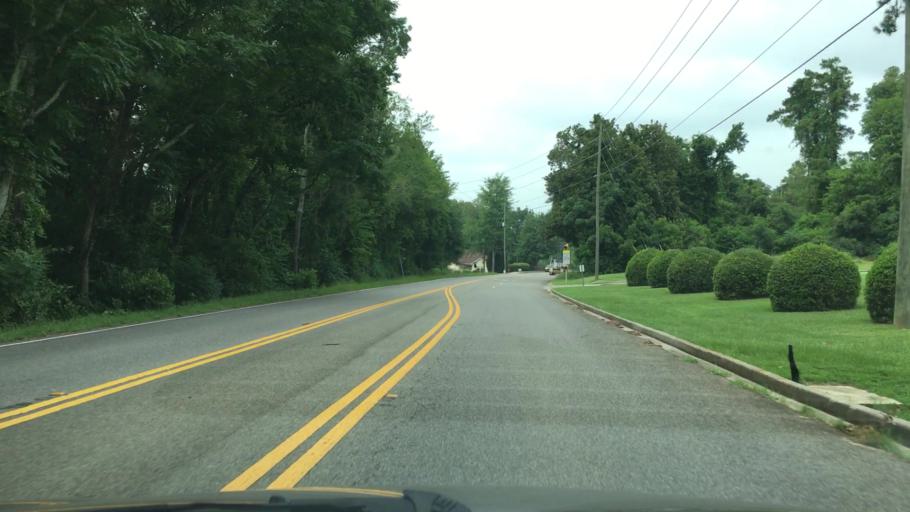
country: US
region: South Carolina
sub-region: Aiken County
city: Belvedere
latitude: 33.5451
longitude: -81.9589
